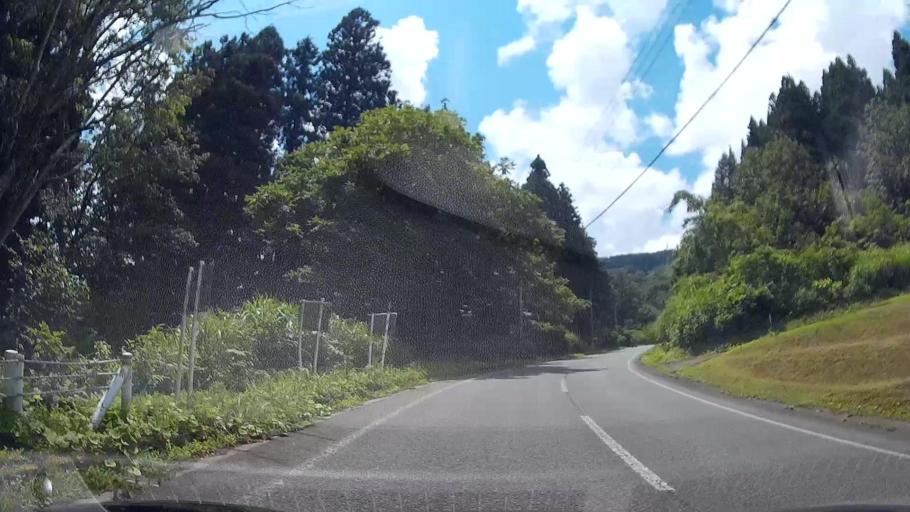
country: JP
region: Niigata
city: Shiozawa
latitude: 37.0235
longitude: 138.8024
